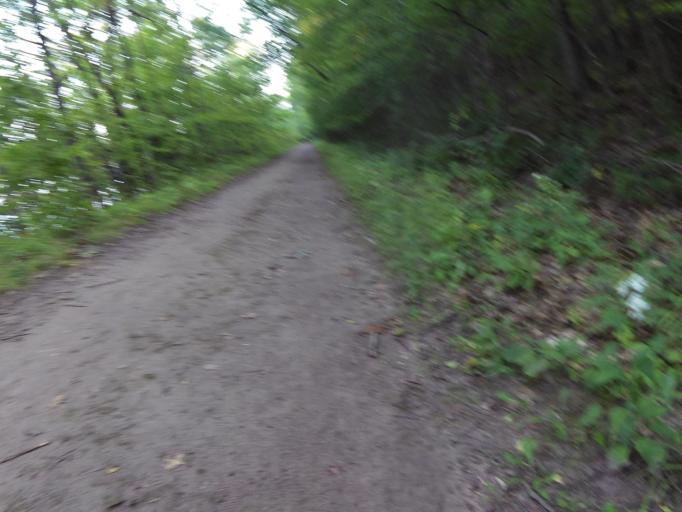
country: US
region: Minnesota
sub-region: Washington County
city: Afton
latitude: 44.8499
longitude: -92.7718
